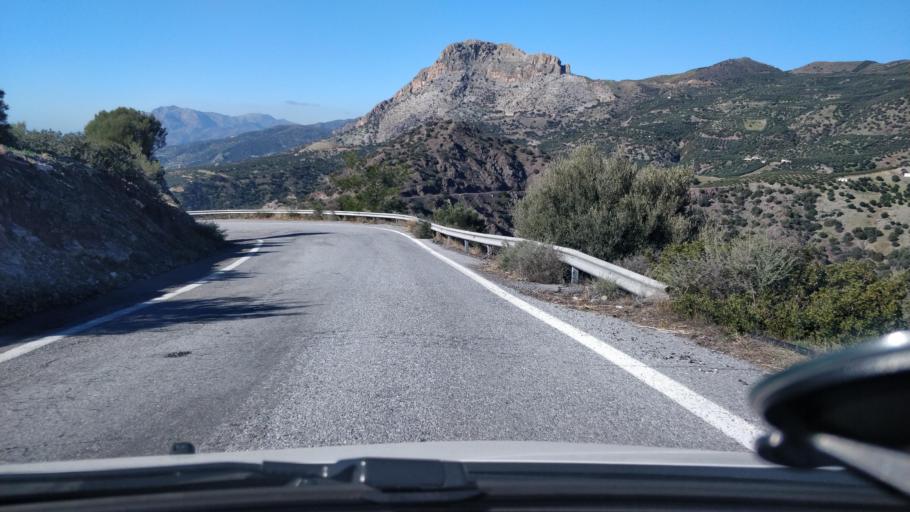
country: GR
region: Crete
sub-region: Nomos Irakleiou
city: Arkalochori
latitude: 35.0066
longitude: 25.4337
